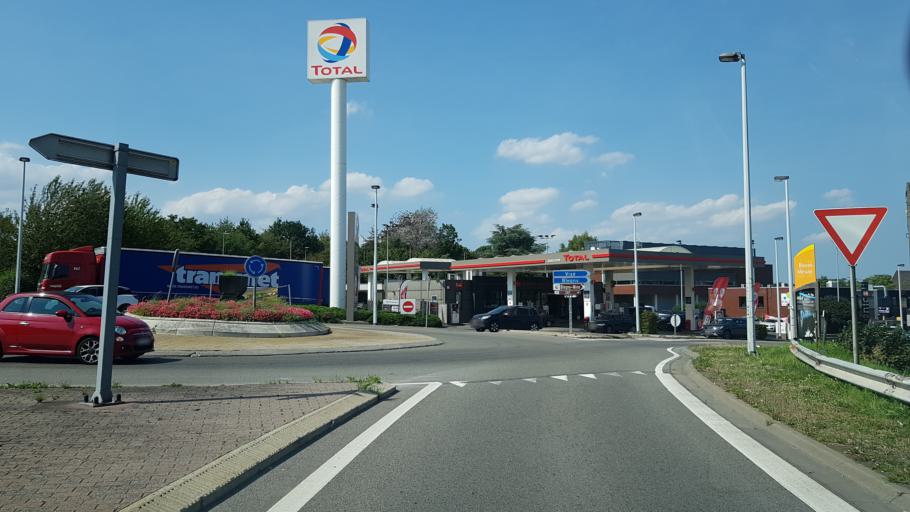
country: BE
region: Wallonia
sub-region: Province de Liege
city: Blegny
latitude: 50.6665
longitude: 5.6937
